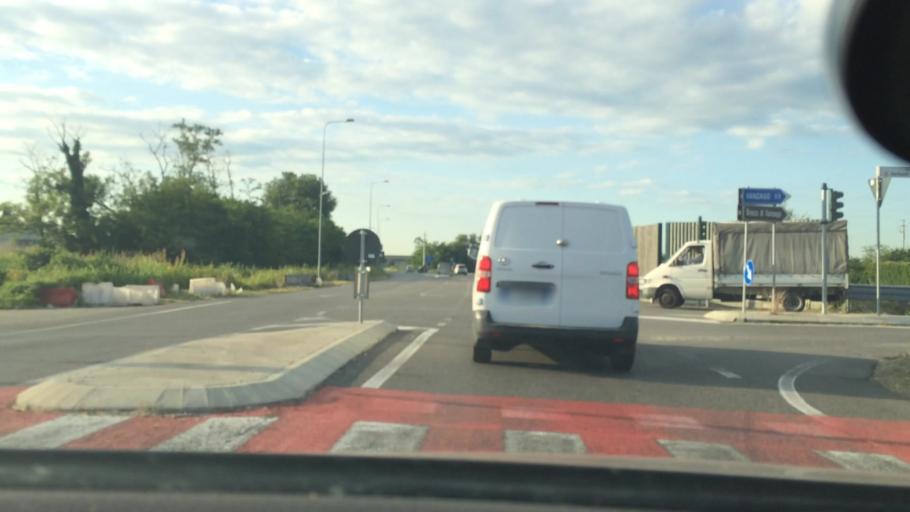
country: IT
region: Lombardy
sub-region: Citta metropolitana di Milano
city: Pogliano Milanese
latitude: 45.5306
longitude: 9.0051
